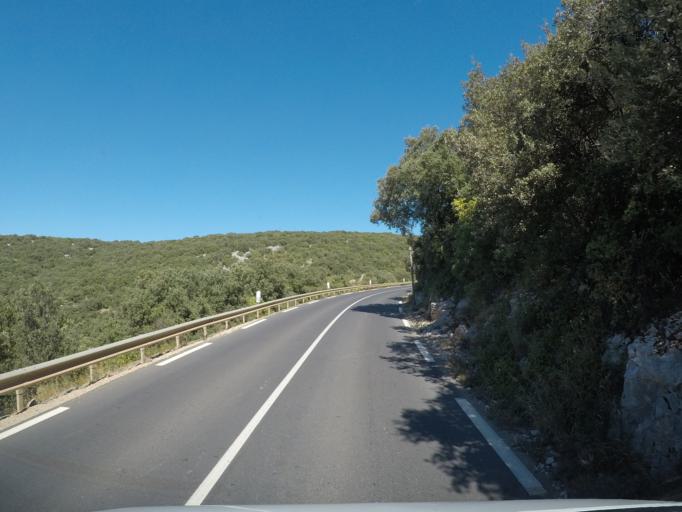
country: FR
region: Languedoc-Roussillon
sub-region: Departement de l'Herault
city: Aniane
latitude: 43.7244
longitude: 3.6283
